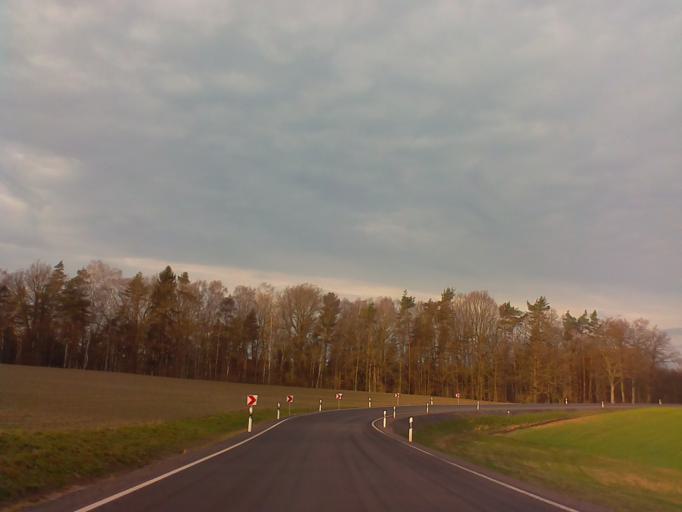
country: DE
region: Thuringia
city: Lindig
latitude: 50.7703
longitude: 11.6040
